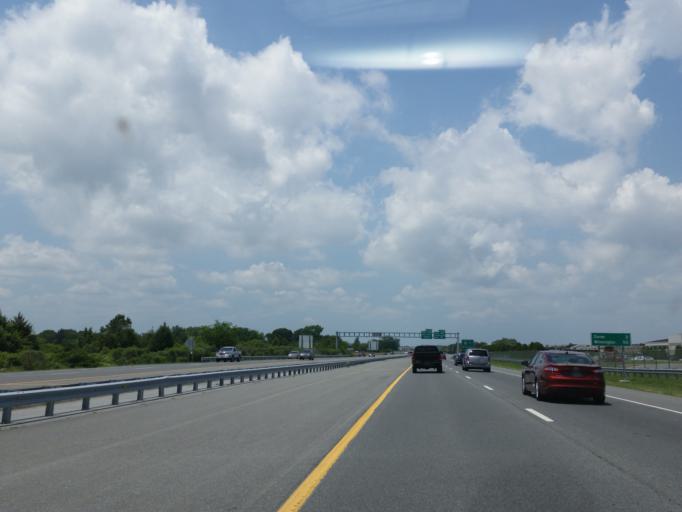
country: US
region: Delaware
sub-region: Kent County
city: Dover Base Housing
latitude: 39.1138
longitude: -75.4668
